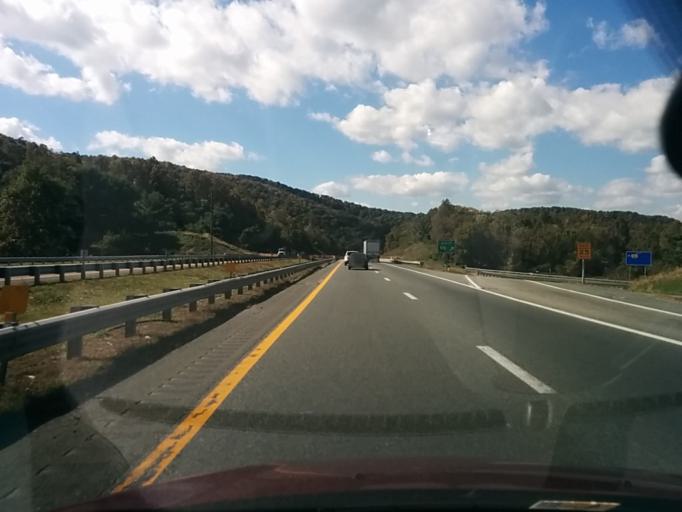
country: US
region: Virginia
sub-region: City of Waynesboro
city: Waynesboro
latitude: 38.0327
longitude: -78.8602
